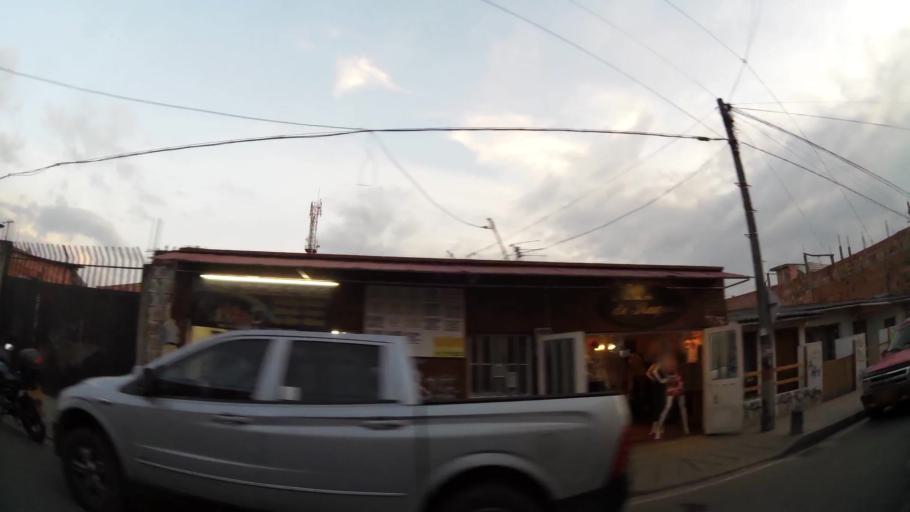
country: CO
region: Cundinamarca
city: Funza
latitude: 4.7144
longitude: -74.2139
